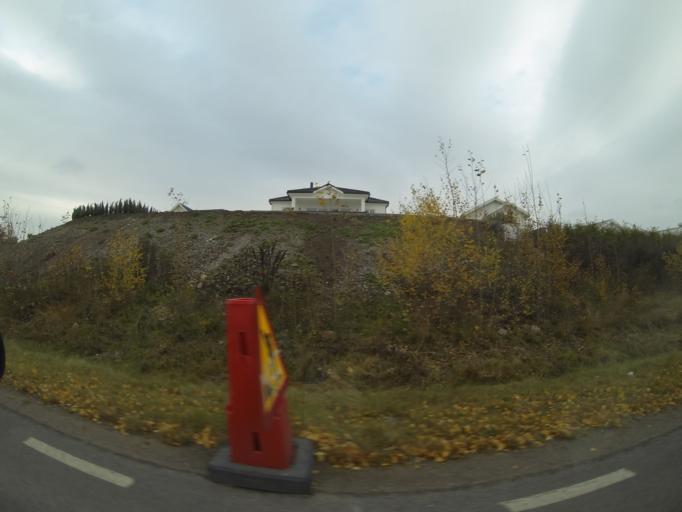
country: SE
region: Vaestmanland
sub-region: Vasteras
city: Vasteras
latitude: 59.6302
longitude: 16.4987
